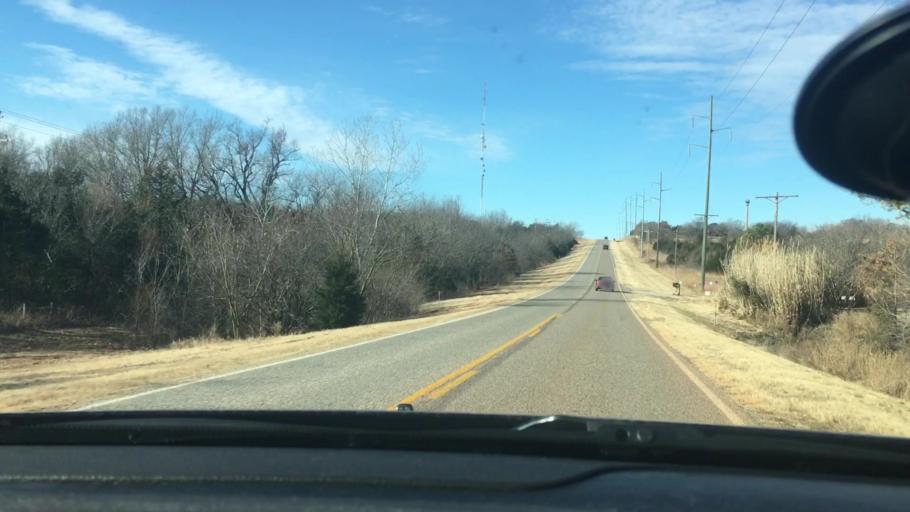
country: US
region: Oklahoma
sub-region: Cleveland County
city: Lexington
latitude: 35.0150
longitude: -97.1795
